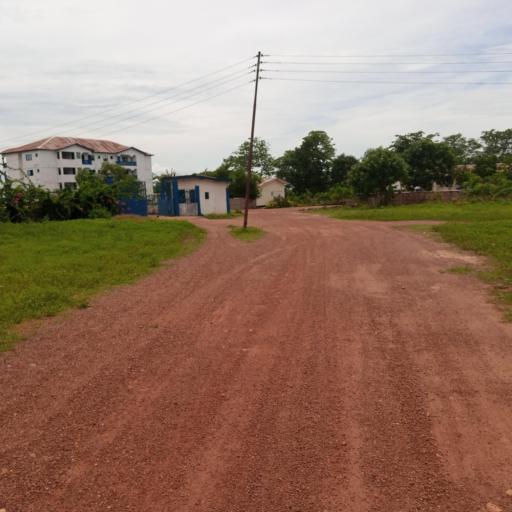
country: SL
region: Southern Province
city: Largo
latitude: 8.1115
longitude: -12.0793
